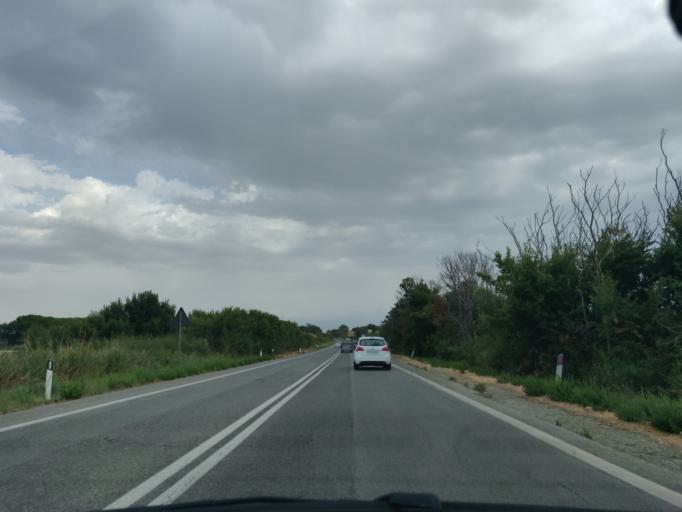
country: IT
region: Latium
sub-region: Citta metropolitana di Roma Capitale
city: Santa Marinella
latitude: 42.0343
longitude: 11.9291
